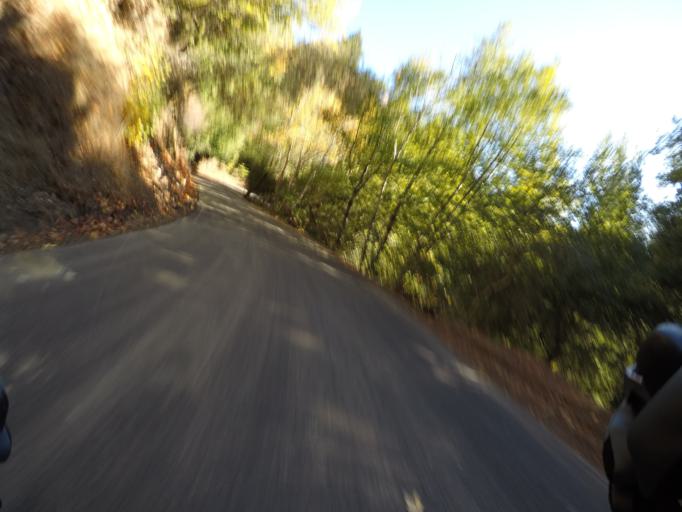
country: US
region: California
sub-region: Santa Clara County
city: Lexington Hills
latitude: 37.1553
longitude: -122.0138
